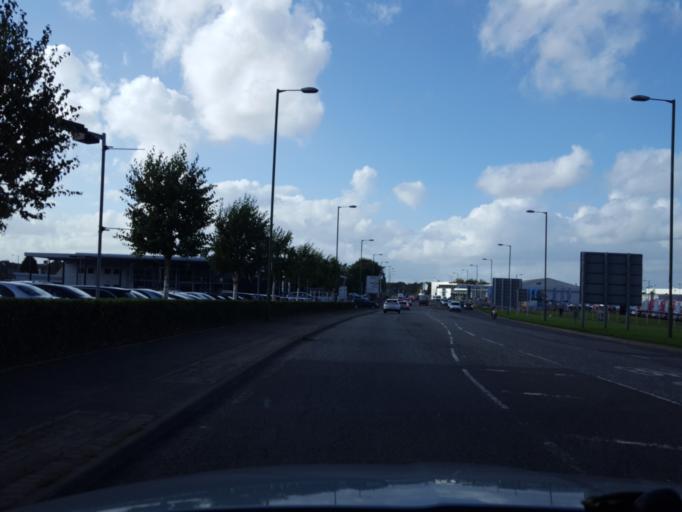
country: GB
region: Scotland
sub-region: Edinburgh
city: Newbridge
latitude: 55.9394
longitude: -3.4039
